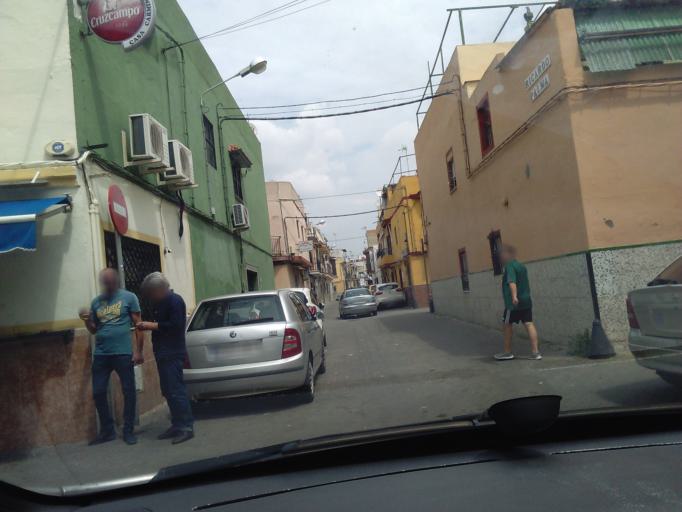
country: ES
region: Andalusia
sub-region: Provincia de Sevilla
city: Sevilla
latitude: 37.3706
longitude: -5.9464
